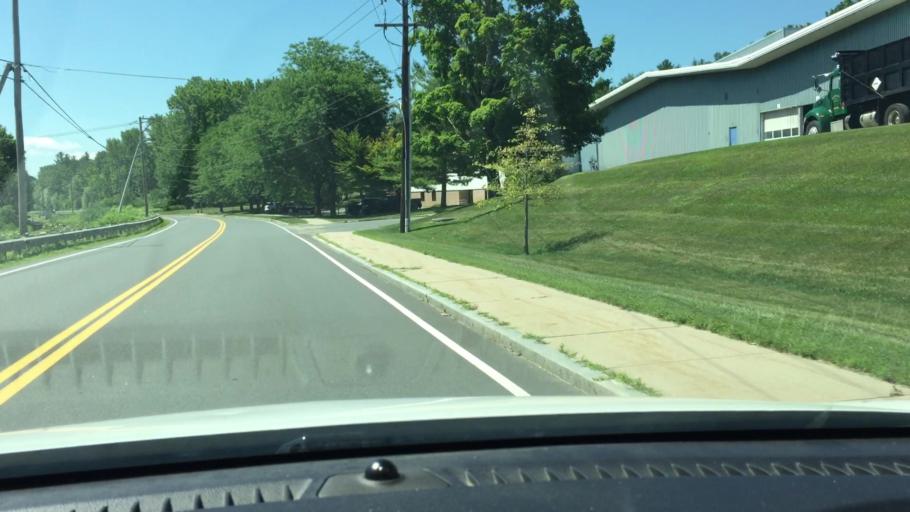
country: US
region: Massachusetts
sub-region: Berkshire County
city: Lenox
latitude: 42.3462
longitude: -73.2460
